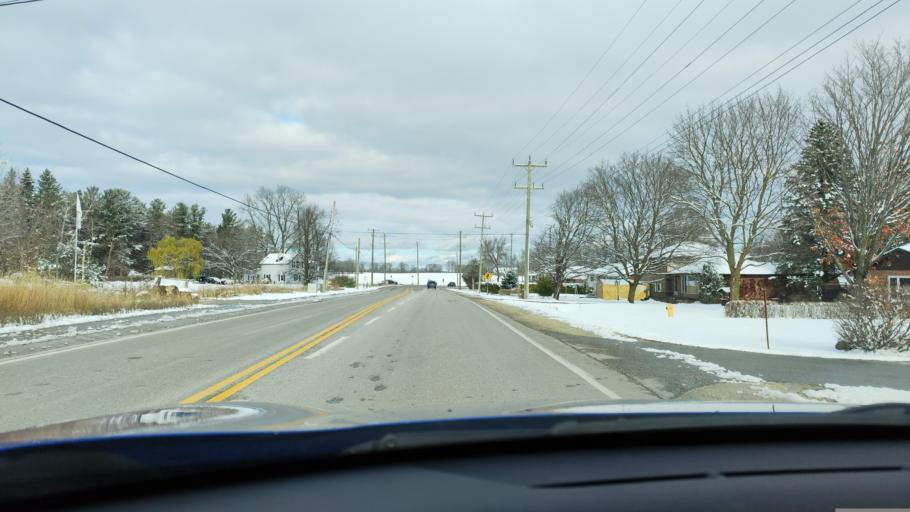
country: CA
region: Ontario
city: Barrie
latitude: 44.3899
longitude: -79.7554
